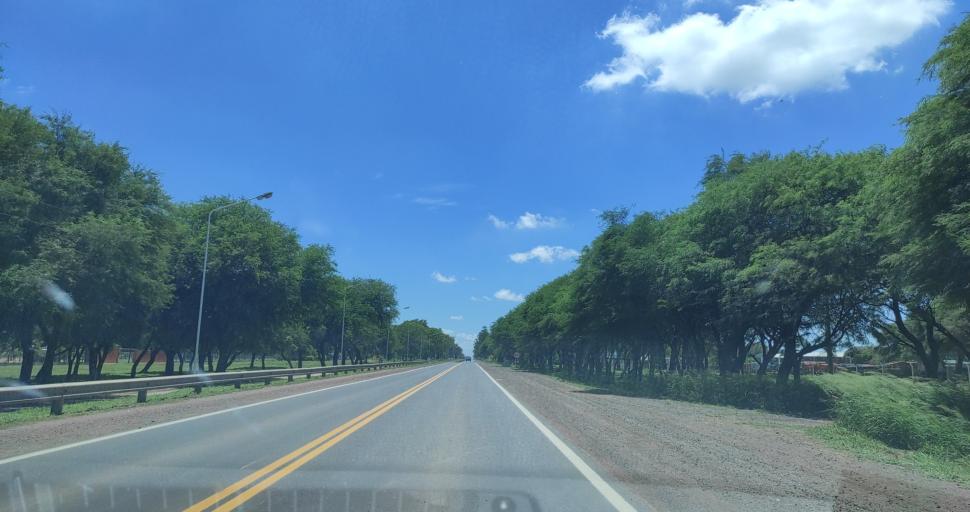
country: AR
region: Chaco
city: Las Brenas
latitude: -27.1035
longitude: -61.0700
